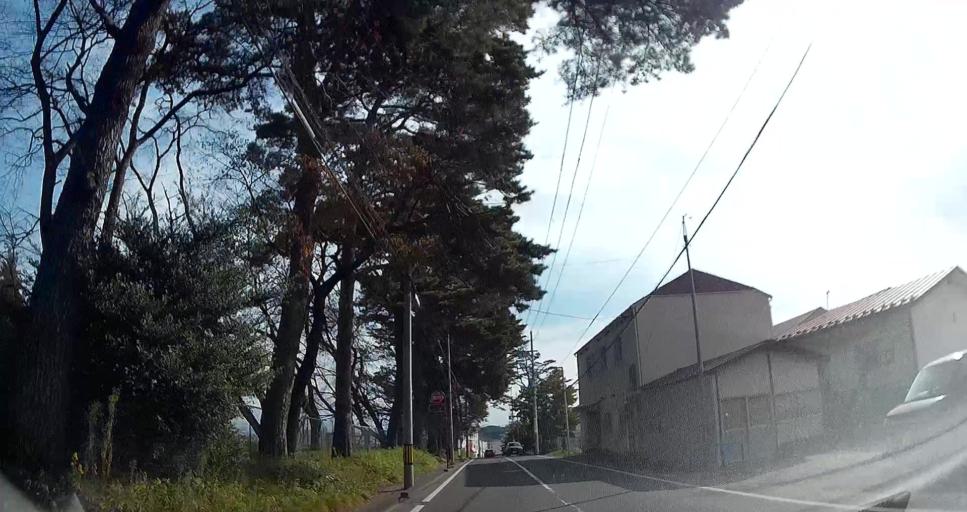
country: JP
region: Miyagi
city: Sendai
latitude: 38.2456
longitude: 140.8576
